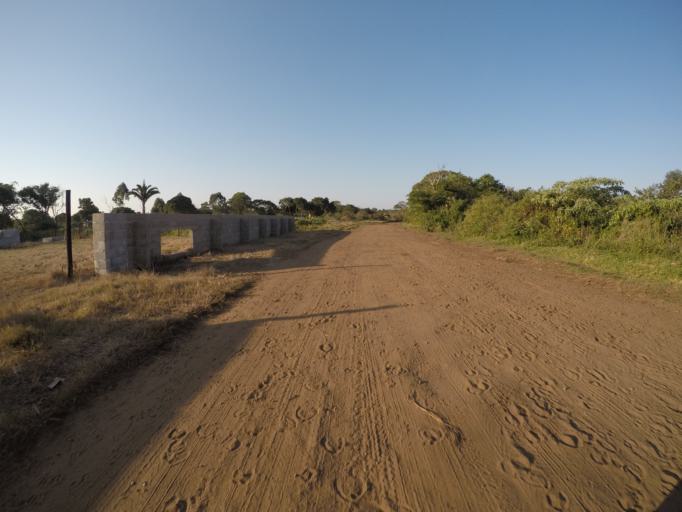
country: ZA
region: KwaZulu-Natal
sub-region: uThungulu District Municipality
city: KwaMbonambi
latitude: -28.6919
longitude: 32.2014
